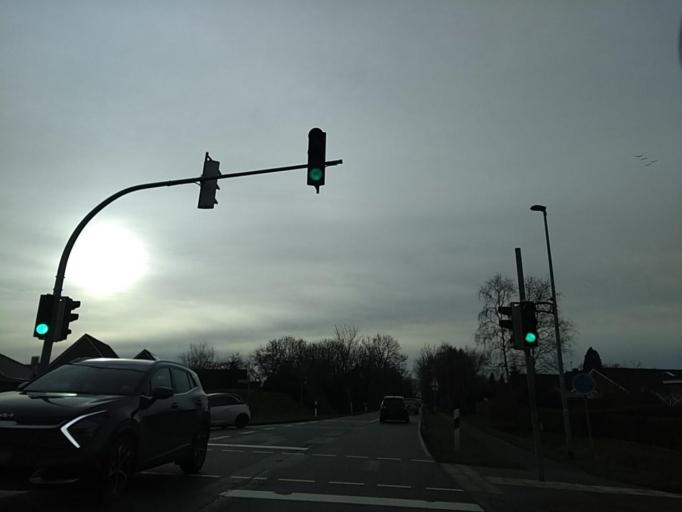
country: DE
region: Lower Saxony
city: Jemgum
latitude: 53.2709
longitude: 7.3864
